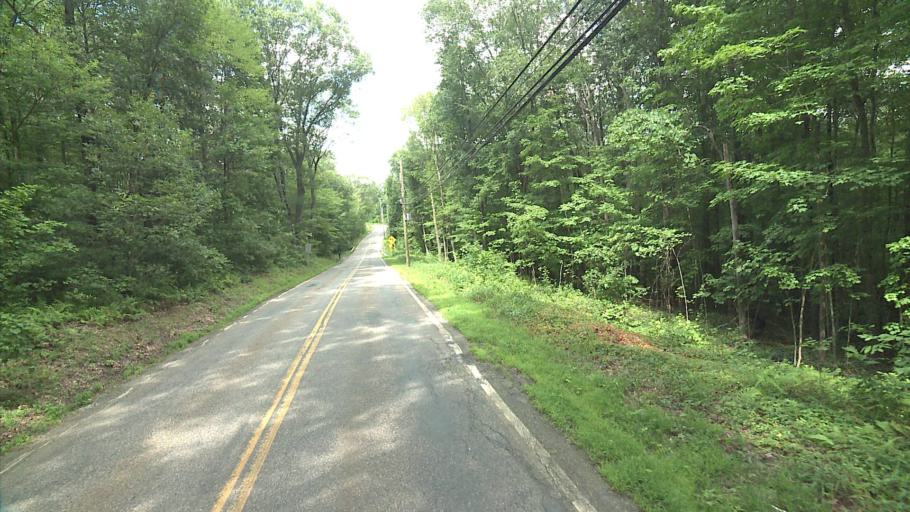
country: US
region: Connecticut
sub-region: Tolland County
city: Stafford
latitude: 41.9533
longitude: -72.1909
